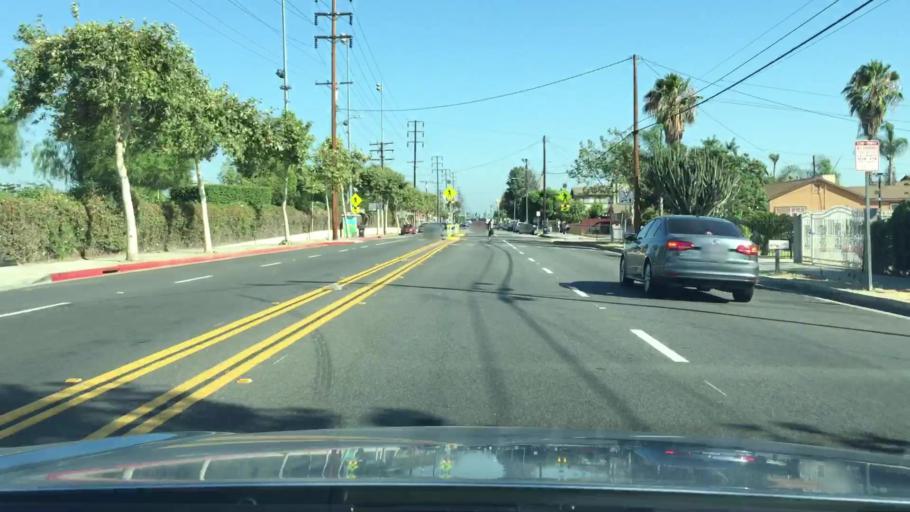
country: US
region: California
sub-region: Los Angeles County
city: Baldwin Park
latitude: 34.0740
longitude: -117.9815
